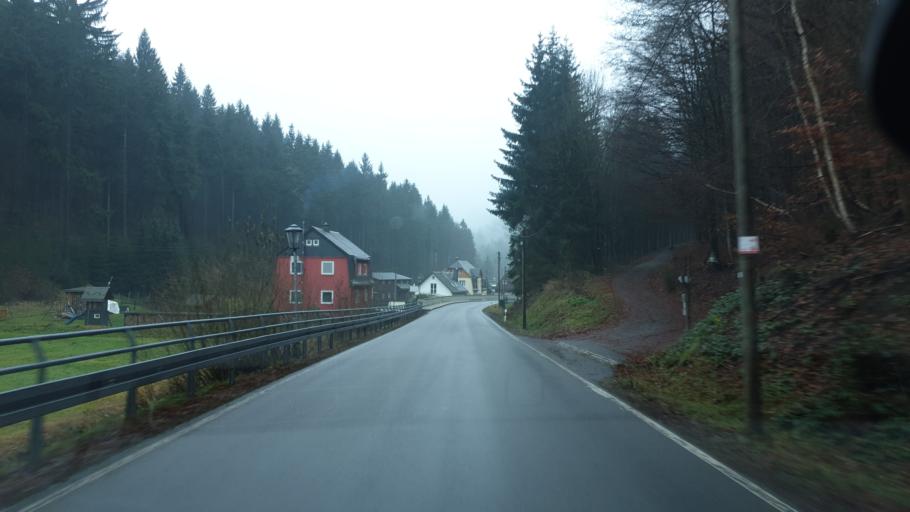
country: DE
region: Saxony
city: Seiffen
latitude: 50.6466
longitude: 13.4378
